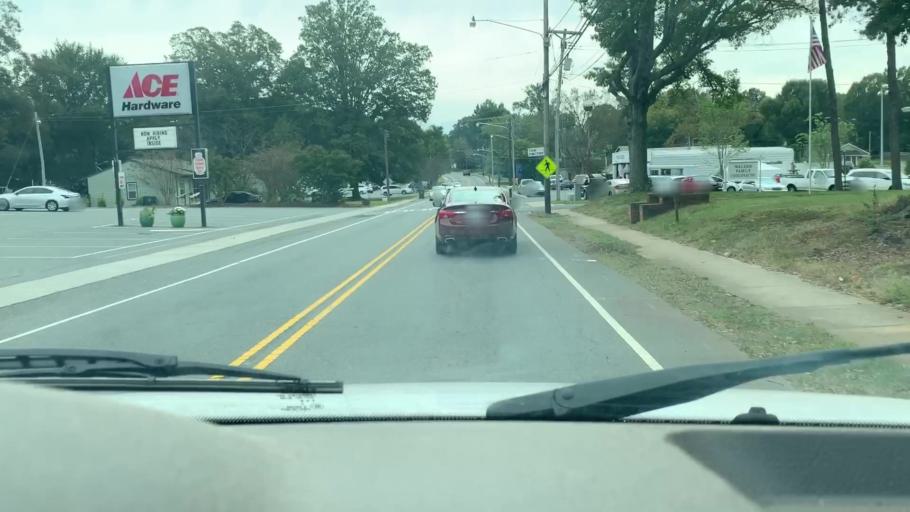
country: US
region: North Carolina
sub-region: Mecklenburg County
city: Cornelius
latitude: 35.4873
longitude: -80.8584
